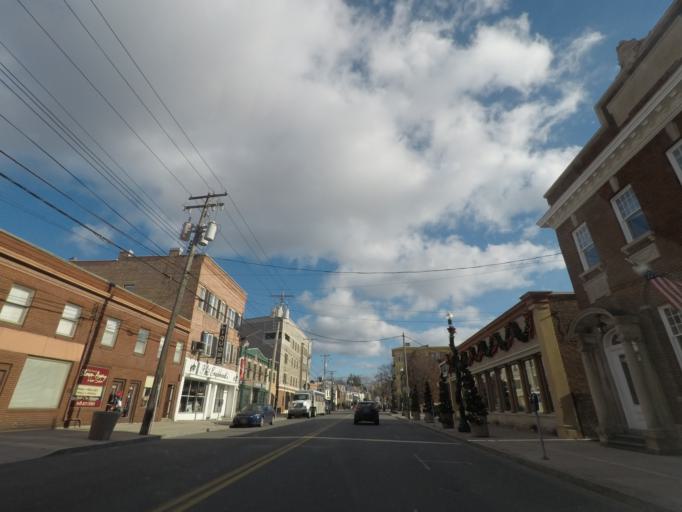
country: US
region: New York
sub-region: Schenectady County
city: Schenectady
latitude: 42.8162
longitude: -73.9387
